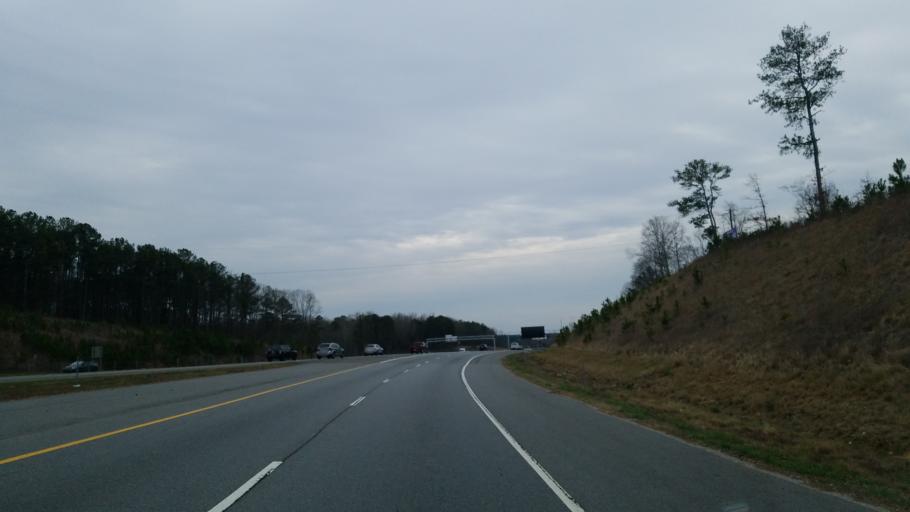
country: US
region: Georgia
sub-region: Cherokee County
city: Holly Springs
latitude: 34.1439
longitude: -84.5184
